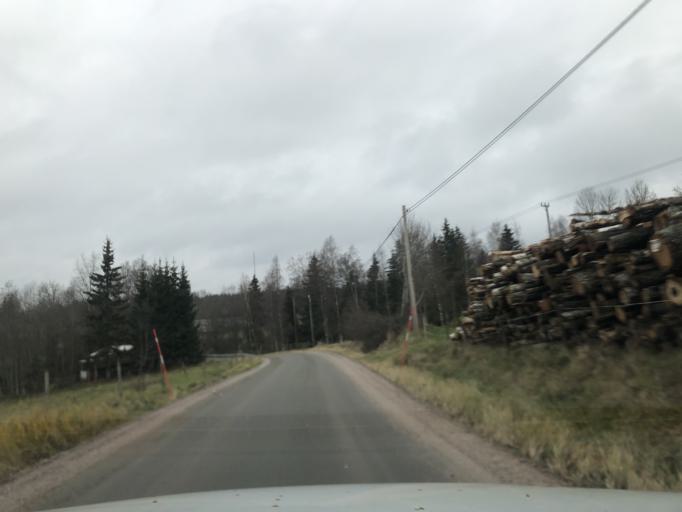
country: SE
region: Vaestra Goetaland
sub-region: Ulricehamns Kommun
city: Ulricehamn
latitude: 57.8618
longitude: 13.5742
